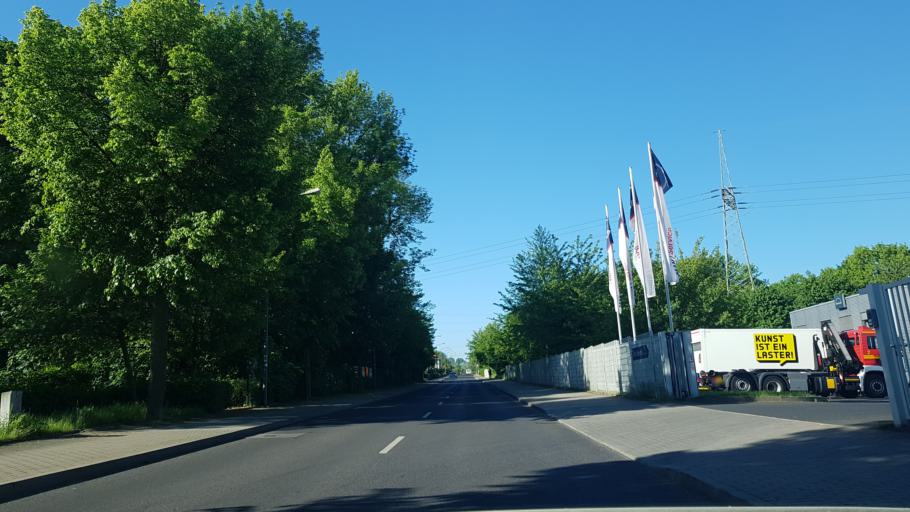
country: DE
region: Saxony
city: Kreischa
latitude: 50.9999
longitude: 13.7924
